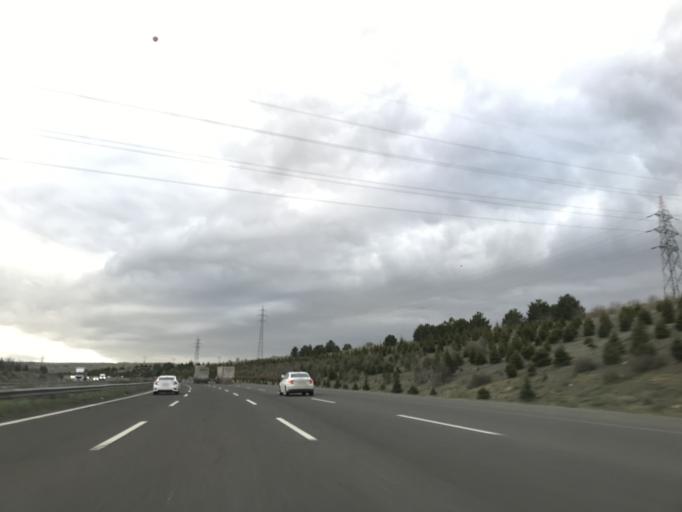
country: TR
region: Ankara
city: Etimesgut
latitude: 39.8071
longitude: 32.6439
